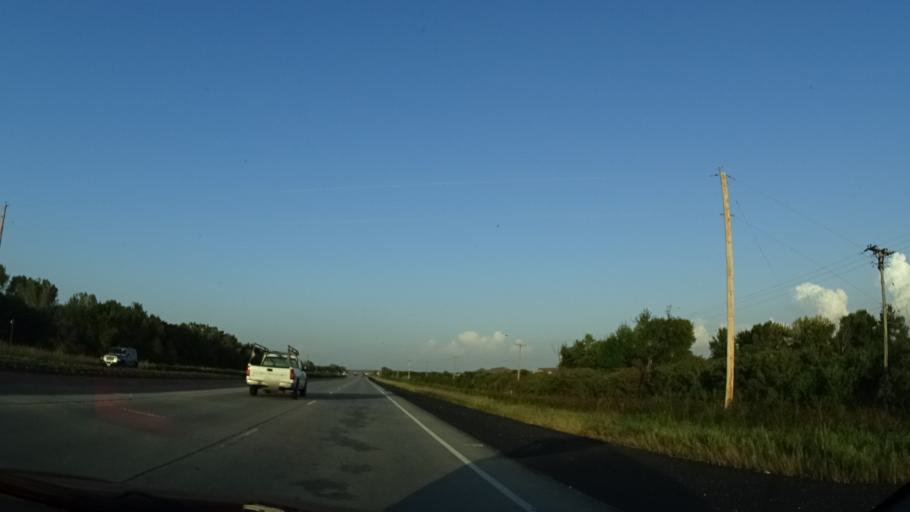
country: US
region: Nebraska
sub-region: Douglas County
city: Omaha
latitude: 41.2084
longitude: -95.9079
